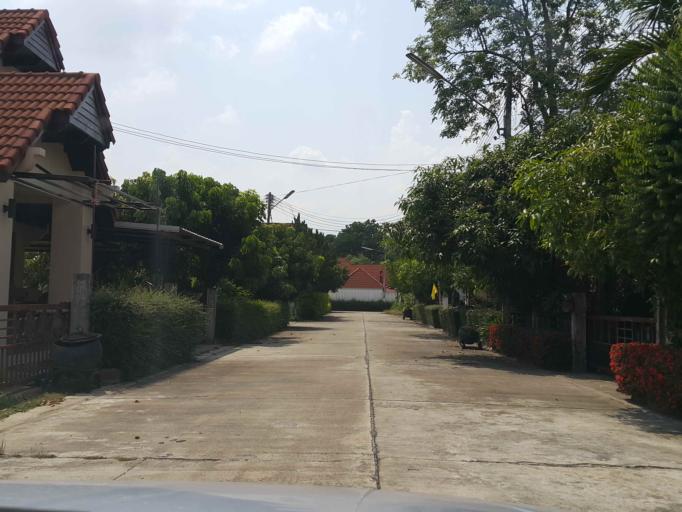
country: TH
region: Chiang Mai
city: Hang Dong
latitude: 18.7076
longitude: 98.9483
